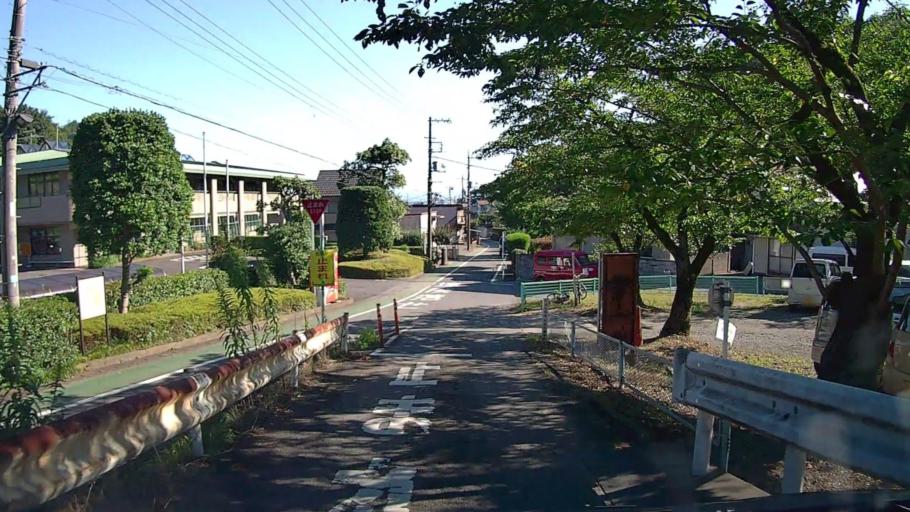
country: JP
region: Tokyo
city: Fussa
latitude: 35.7722
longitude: 139.3618
